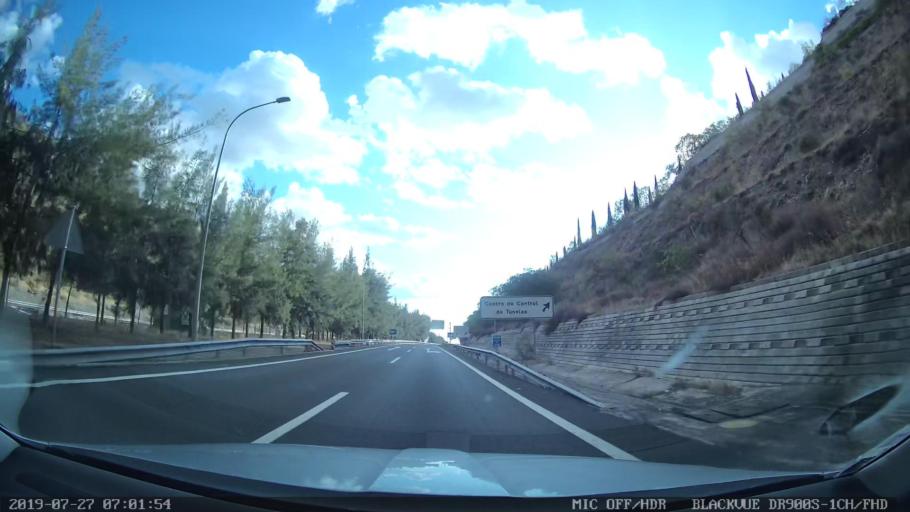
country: ES
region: Extremadura
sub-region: Provincia de Caceres
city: Casas de Miravete
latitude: 39.6901
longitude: -5.7078
